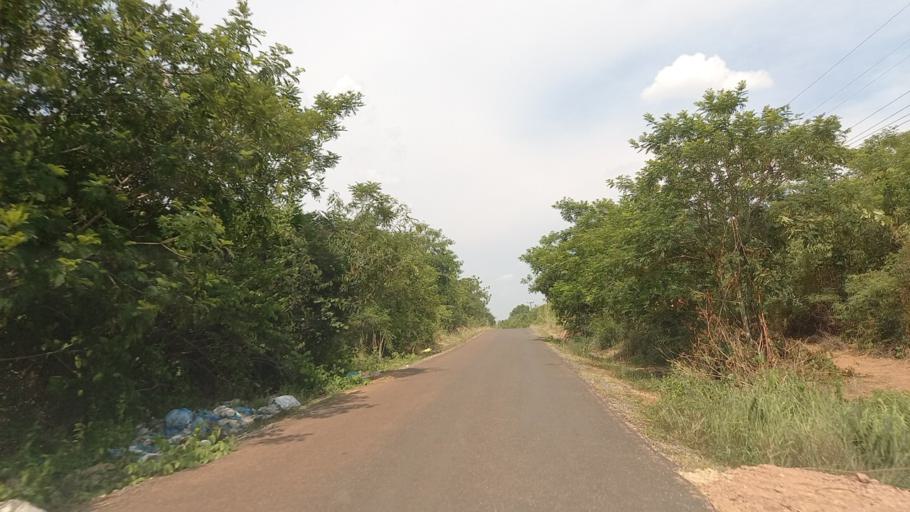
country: LA
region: Bolikhamxai
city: Muang Pakxan
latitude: 18.4288
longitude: 103.7301
